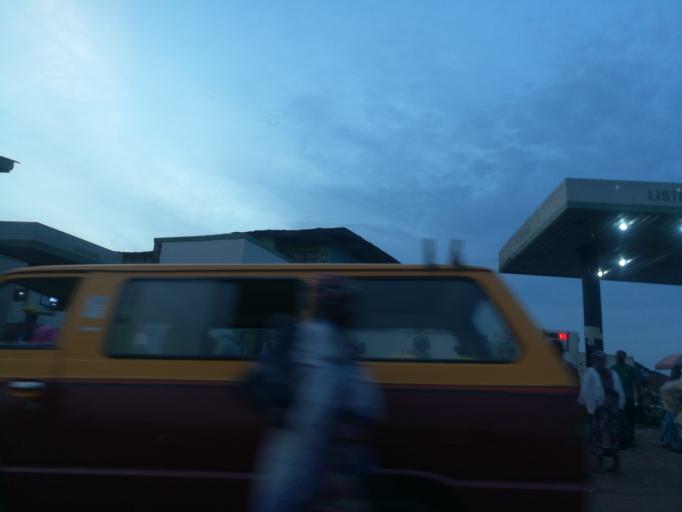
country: NG
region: Oyo
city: Ibadan
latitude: 7.3790
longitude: 3.8988
